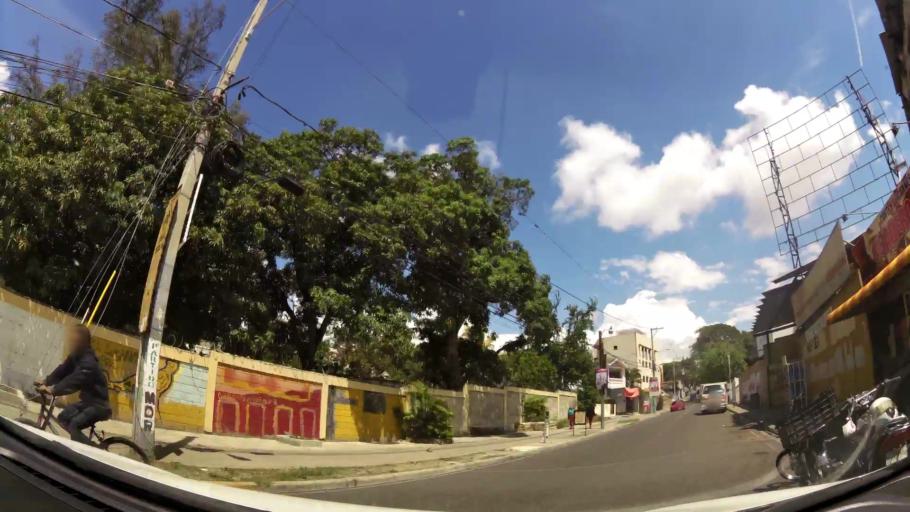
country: DO
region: Santiago
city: Santiago de los Caballeros
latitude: 19.4625
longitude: -70.6773
